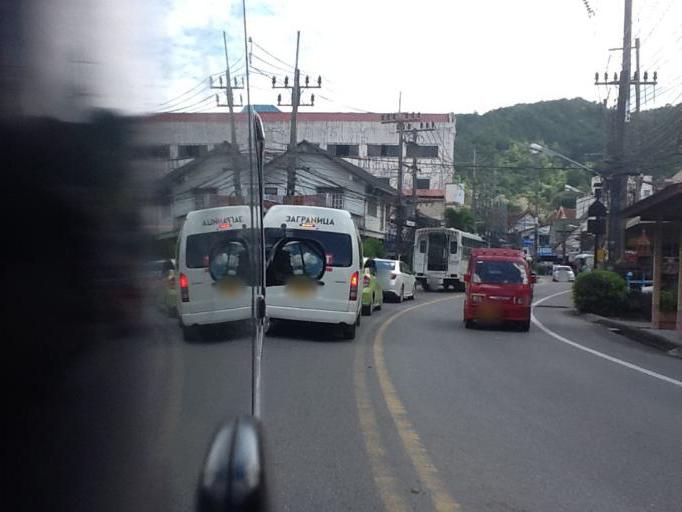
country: TH
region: Phuket
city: Patong
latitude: 7.9028
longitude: 98.3083
